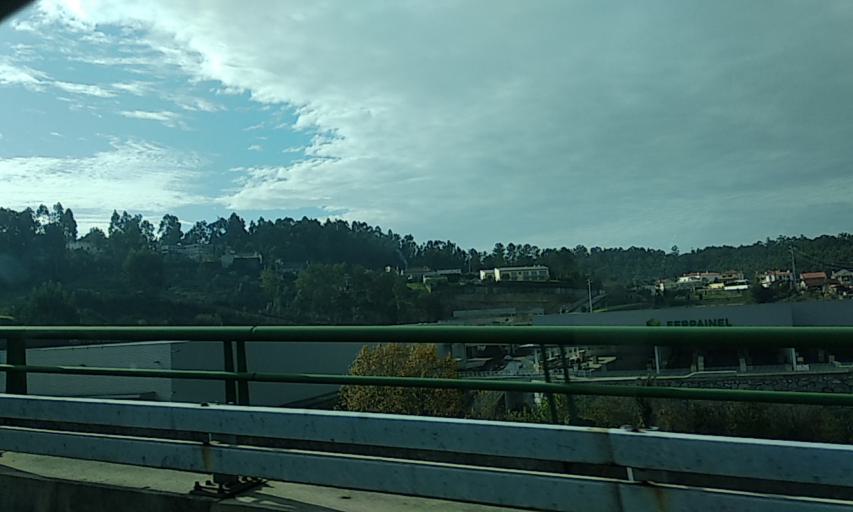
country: PT
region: Braga
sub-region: Braga
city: Oliveira
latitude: 41.4972
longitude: -8.4694
